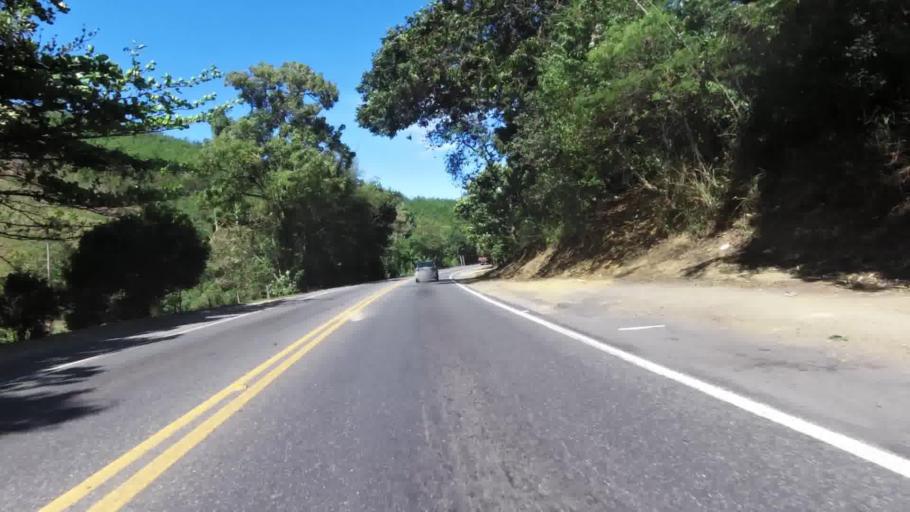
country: BR
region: Espirito Santo
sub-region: Iconha
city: Iconha
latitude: -20.8311
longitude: -40.8592
